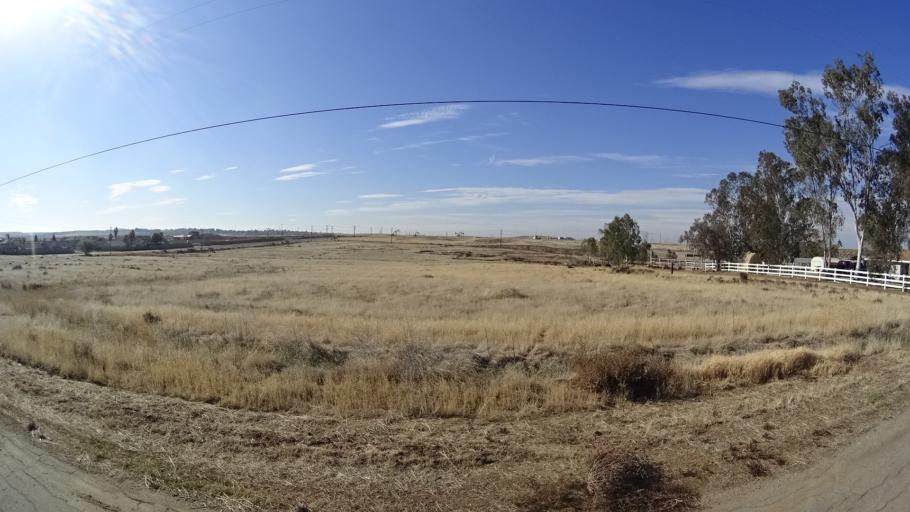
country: US
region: California
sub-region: Kern County
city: Oildale
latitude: 35.4143
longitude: -118.8984
